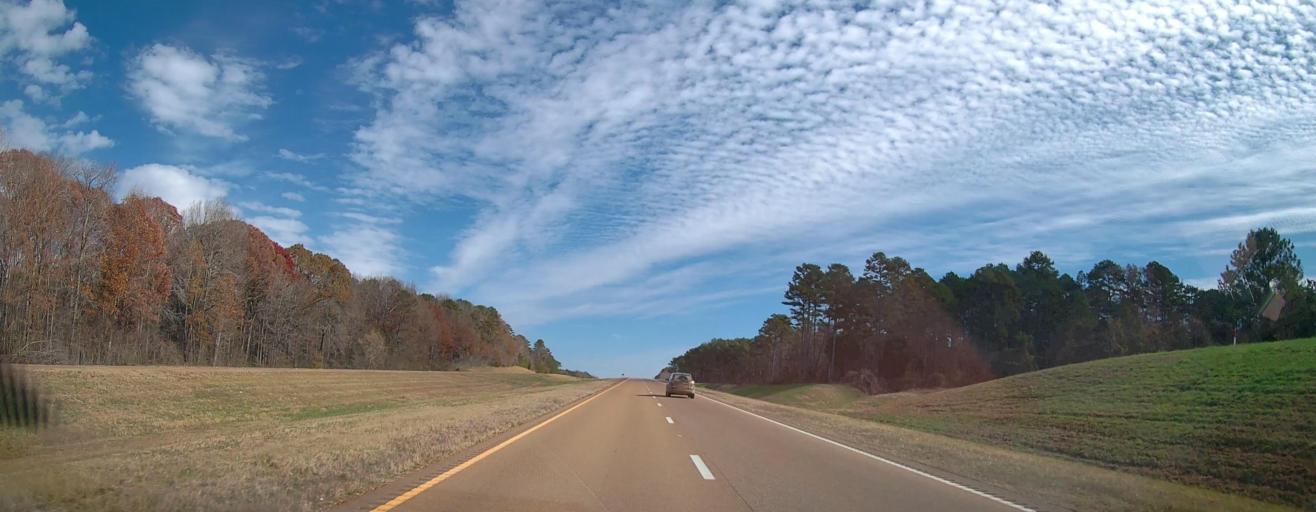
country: US
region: Mississippi
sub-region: Benton County
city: Ashland
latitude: 34.9531
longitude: -89.0452
